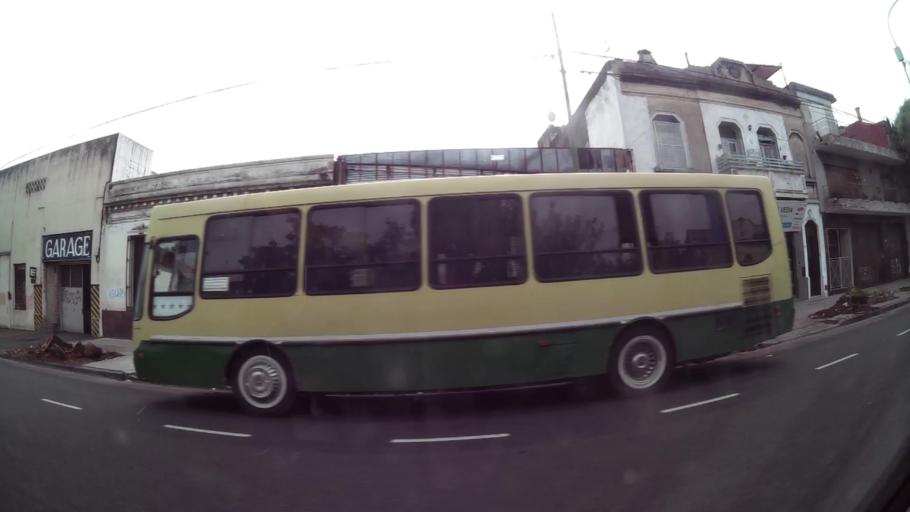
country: AR
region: Buenos Aires F.D.
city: Villa Santa Rita
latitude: -34.6309
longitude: -58.4334
